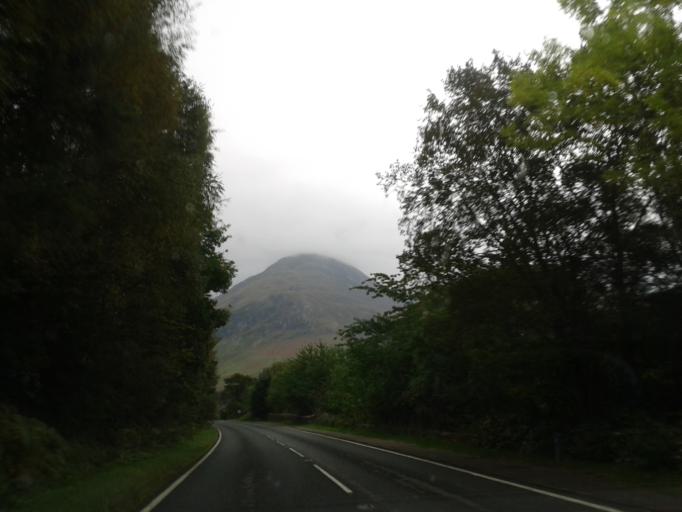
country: GB
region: Scotland
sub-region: Highland
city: Fort William
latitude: 57.2343
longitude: -5.4274
